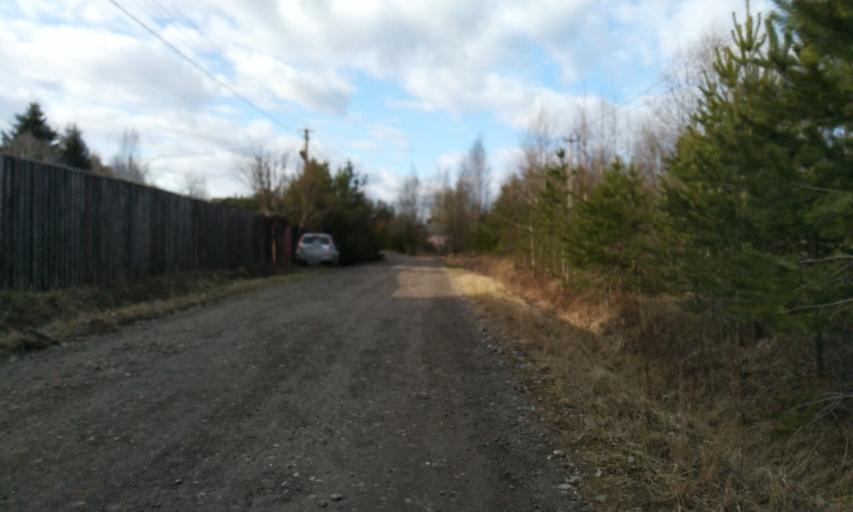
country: RU
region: Leningrad
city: Toksovo
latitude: 60.1271
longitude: 30.4892
